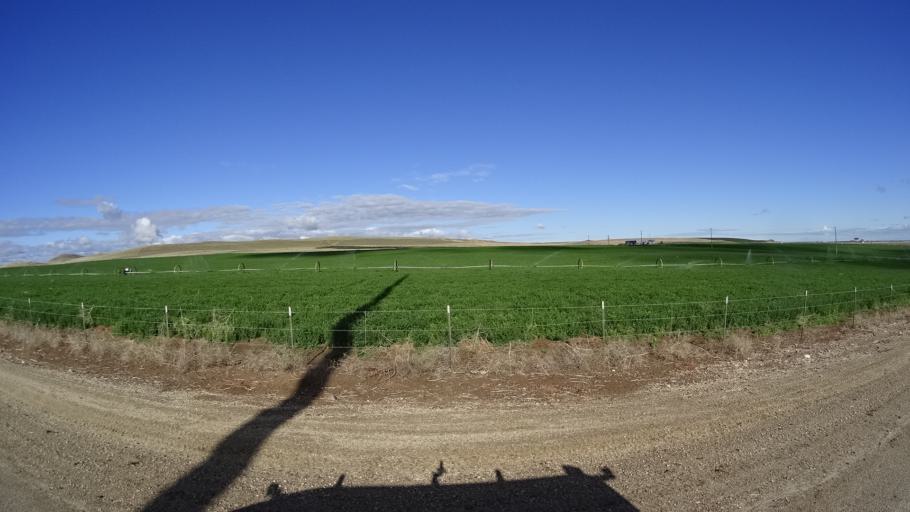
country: US
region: Idaho
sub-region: Ada County
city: Kuna
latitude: 43.4505
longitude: -116.4140
